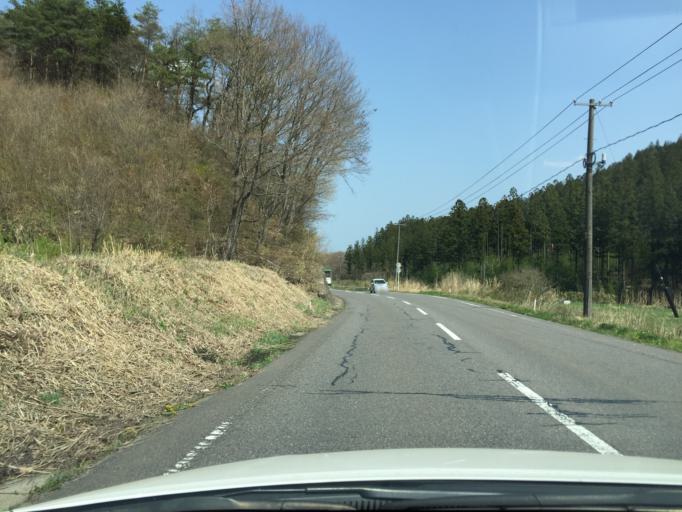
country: JP
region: Fukushima
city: Funehikimachi-funehiki
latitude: 37.4566
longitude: 140.6977
